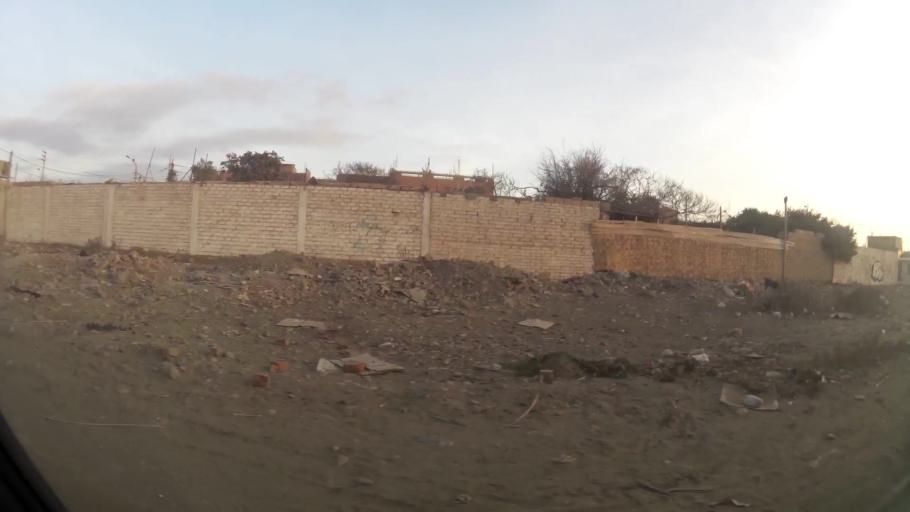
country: PE
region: Lima
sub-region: Huaura
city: Huacho
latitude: -11.1195
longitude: -77.6082
